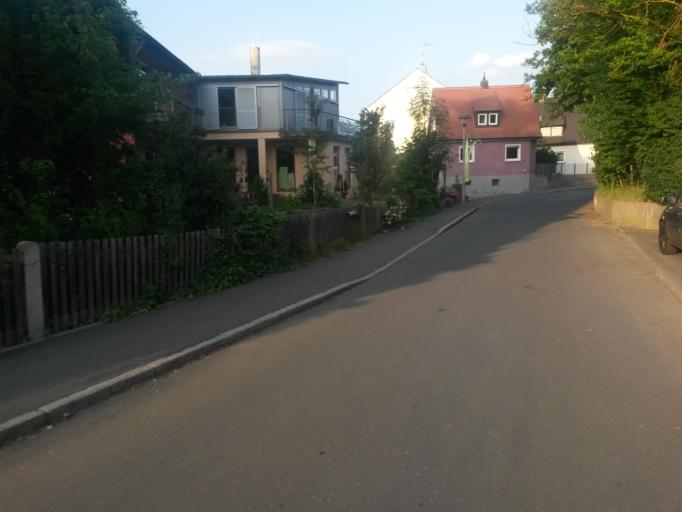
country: DE
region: Bavaria
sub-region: Regierungsbezirk Mittelfranken
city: Rosstal
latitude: 49.4274
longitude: 10.9128
